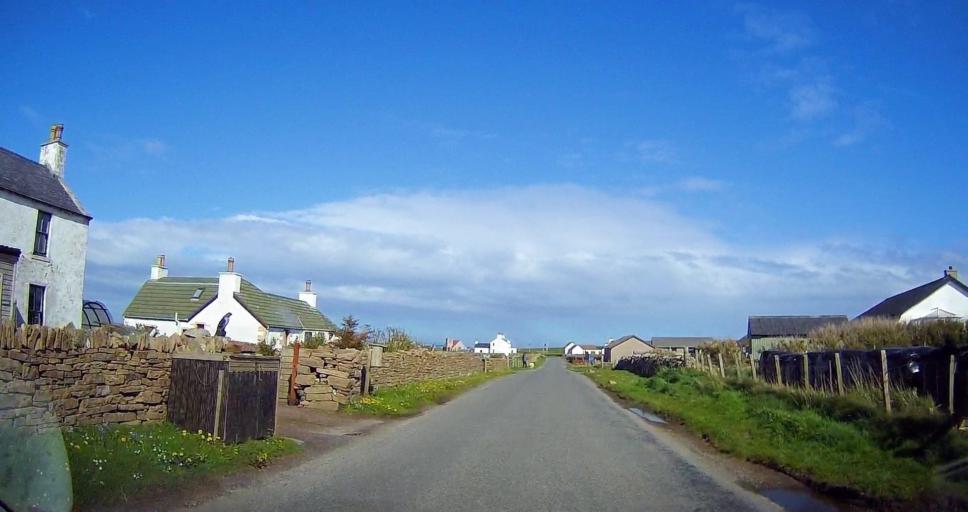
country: GB
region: Scotland
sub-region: Shetland Islands
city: Sandwick
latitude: 59.9168
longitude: -1.3175
